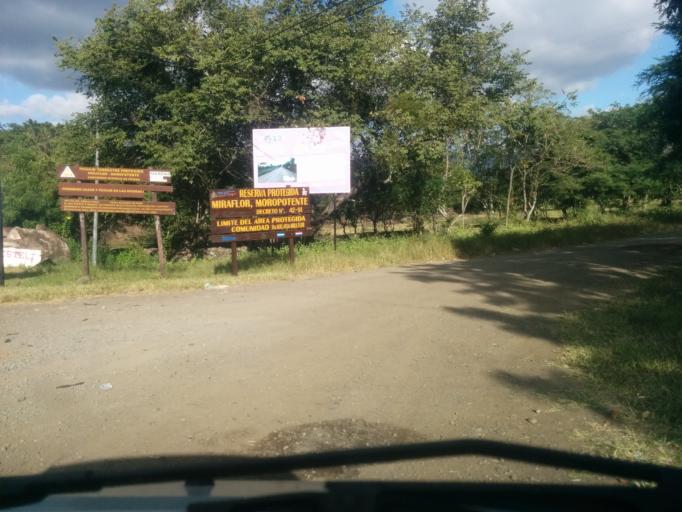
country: NI
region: Esteli
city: Condega
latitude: 13.2429
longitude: -86.3740
